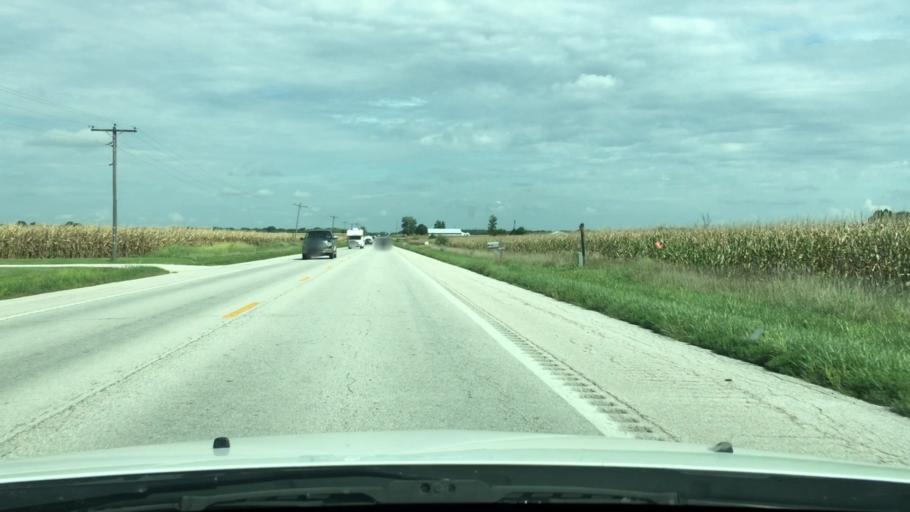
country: US
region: Missouri
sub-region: Montgomery County
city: Wellsville
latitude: 39.1835
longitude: -91.6472
